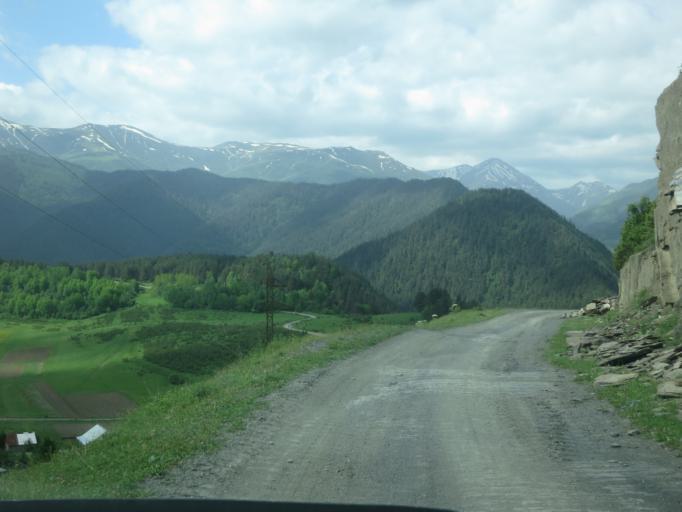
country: RU
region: Chechnya
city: Itum-Kali
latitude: 42.3726
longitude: 45.6297
